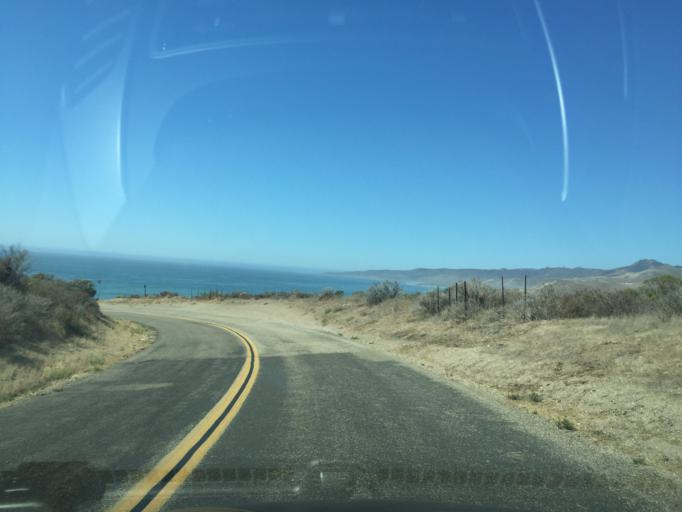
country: US
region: California
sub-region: Santa Barbara County
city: Lompoc
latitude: 34.5106
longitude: -120.4972
